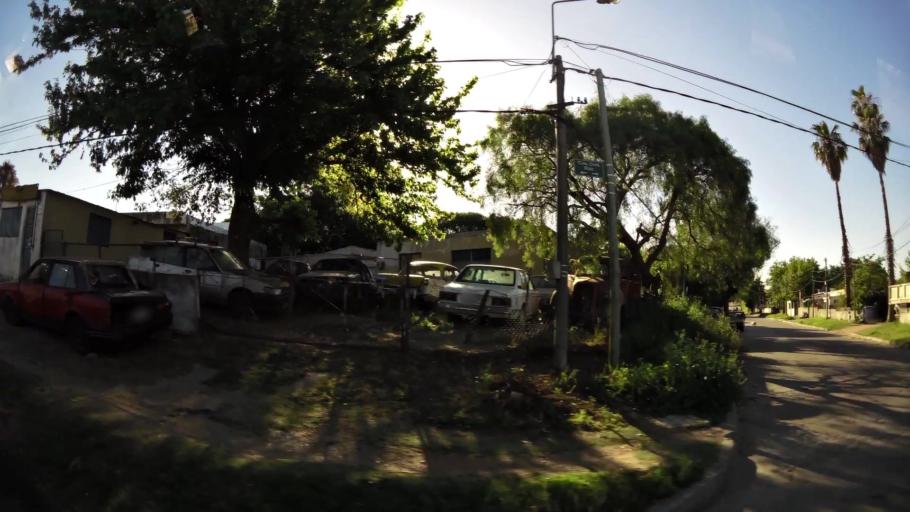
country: UY
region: Montevideo
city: Montevideo
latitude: -34.8333
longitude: -56.2009
